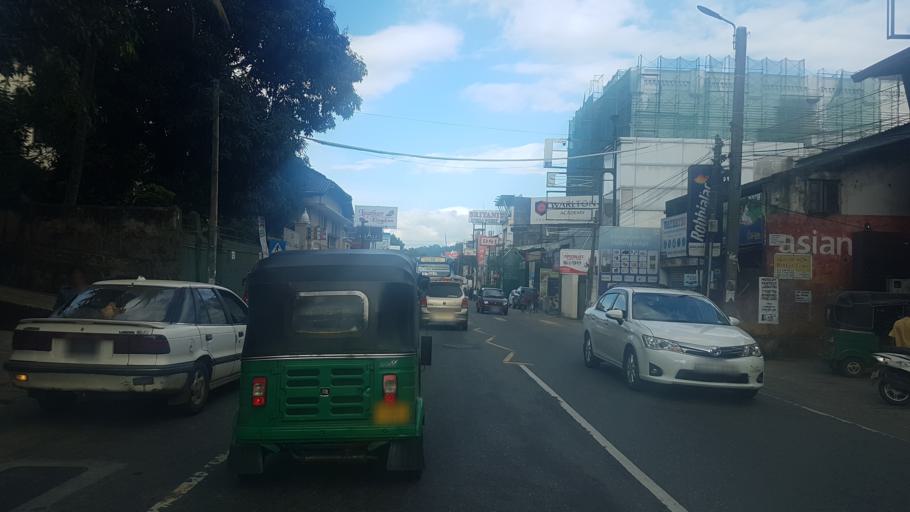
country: LK
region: Central
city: Kandy
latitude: 7.2826
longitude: 80.6221
